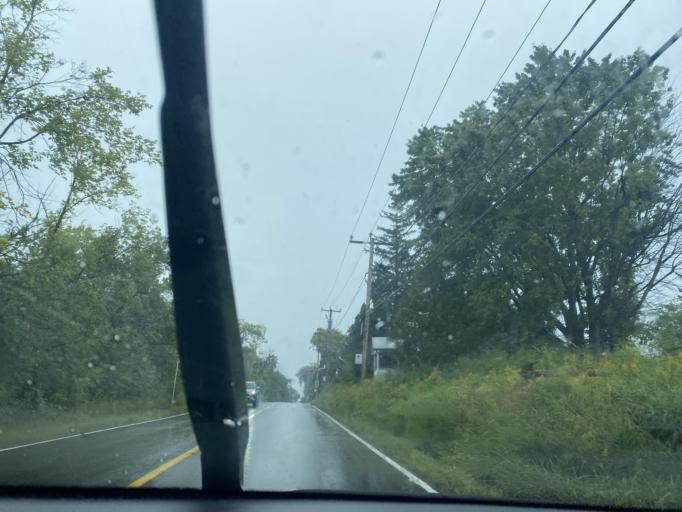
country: CA
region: Quebec
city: Baie-D'Urfe
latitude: 45.4591
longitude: -73.9252
